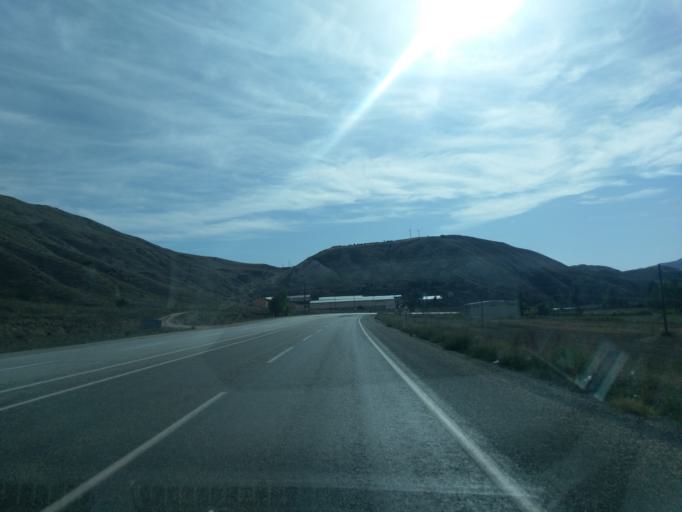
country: TR
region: Sivas
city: Zara
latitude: 39.8594
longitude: 37.8341
